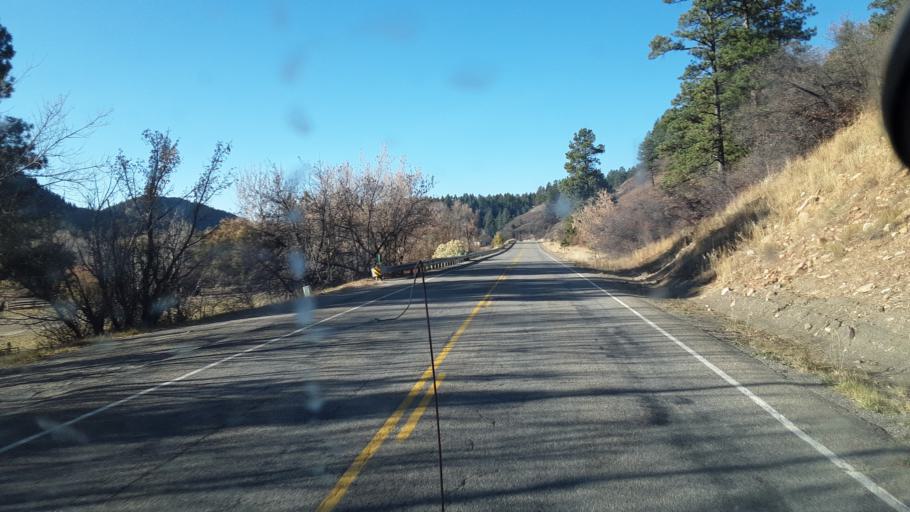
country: US
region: Colorado
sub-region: La Plata County
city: Durango
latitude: 37.3239
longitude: -107.7632
